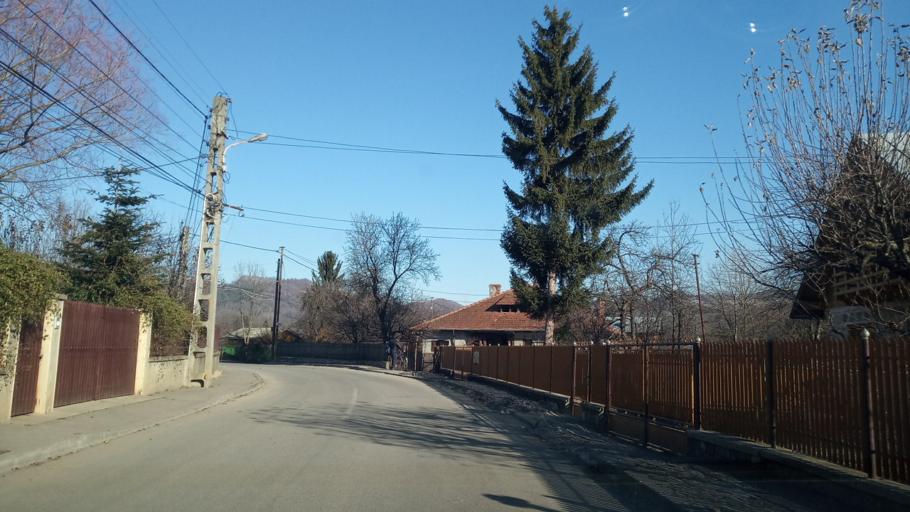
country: RO
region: Prahova
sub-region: Oras Breaza
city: Breaza
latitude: 45.1855
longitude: 25.6668
